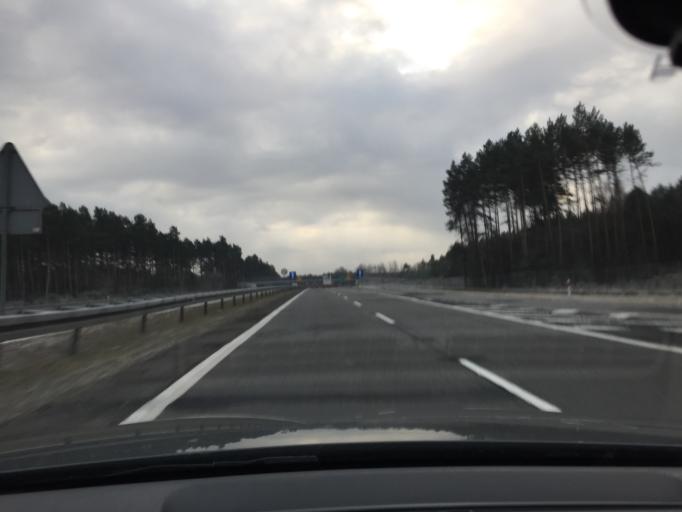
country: PL
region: Lubusz
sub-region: Powiat zarski
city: Trzebiel
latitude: 51.6337
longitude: 14.8745
